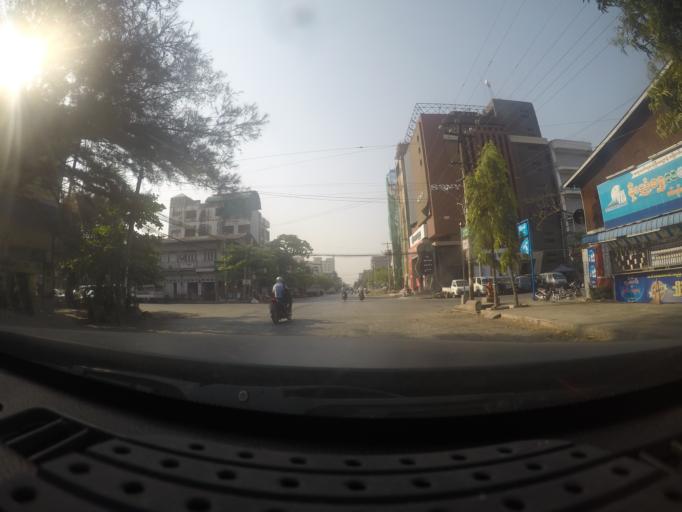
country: MM
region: Mandalay
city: Mandalay
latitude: 21.9774
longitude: 96.0808
